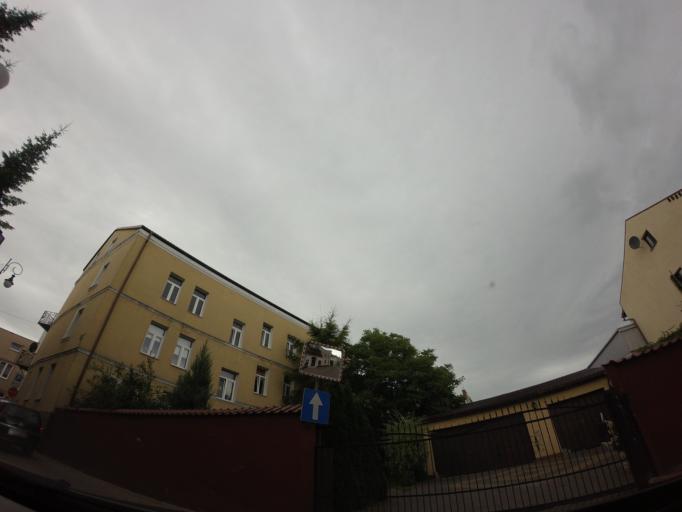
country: PL
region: Masovian Voivodeship
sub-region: Ostroleka
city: Ostroleka
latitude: 53.0820
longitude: 21.5697
